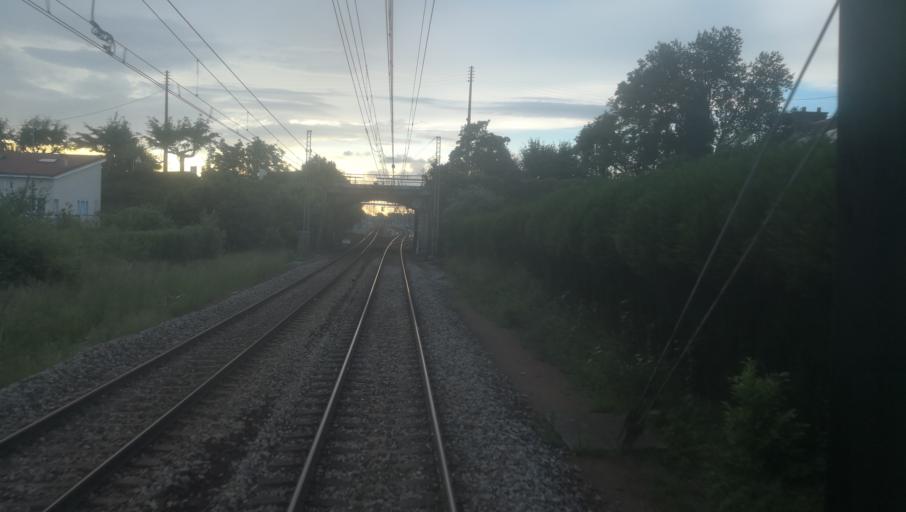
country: FR
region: Limousin
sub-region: Departement de la Creuse
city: La Souterraine
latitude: 46.2385
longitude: 1.4937
